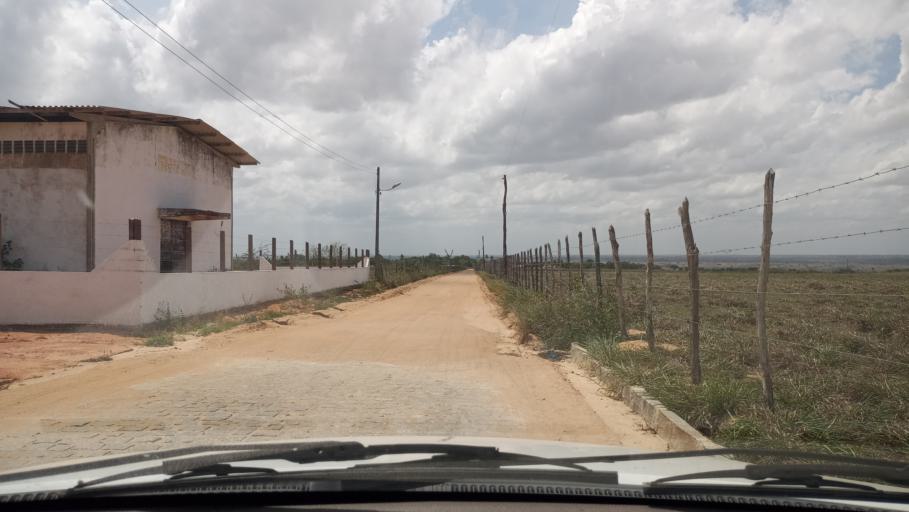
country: BR
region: Rio Grande do Norte
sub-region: Montanhas
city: Montanhas
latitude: -6.3631
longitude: -35.3313
